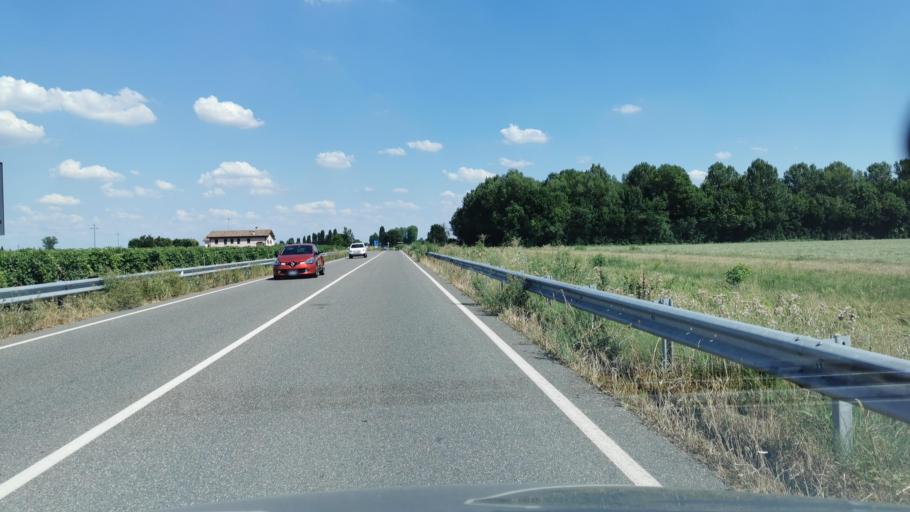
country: IT
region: Emilia-Romagna
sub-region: Provincia di Modena
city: Sam Marino
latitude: 44.7997
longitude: 10.9083
